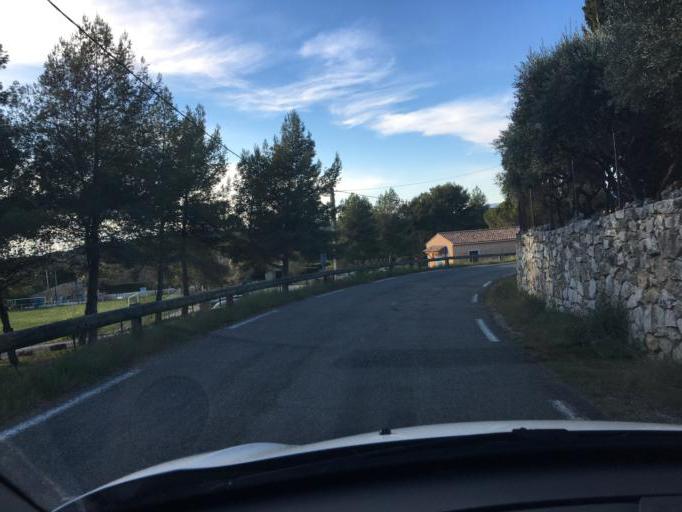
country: FR
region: Provence-Alpes-Cote d'Azur
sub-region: Departement du Vaucluse
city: Villes-sur-Auzon
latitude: 44.0547
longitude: 5.2375
